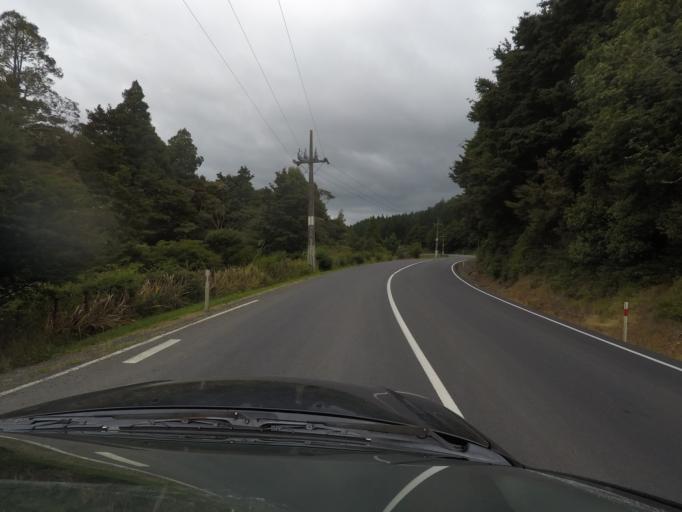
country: NZ
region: Auckland
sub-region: Auckland
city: Wellsford
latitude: -36.2860
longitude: 174.6131
